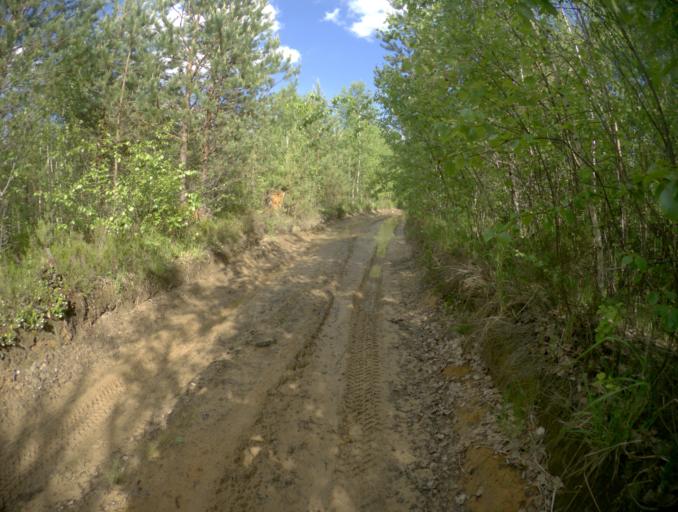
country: RU
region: Vladimir
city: Zolotkovo
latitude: 55.3301
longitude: 40.9764
